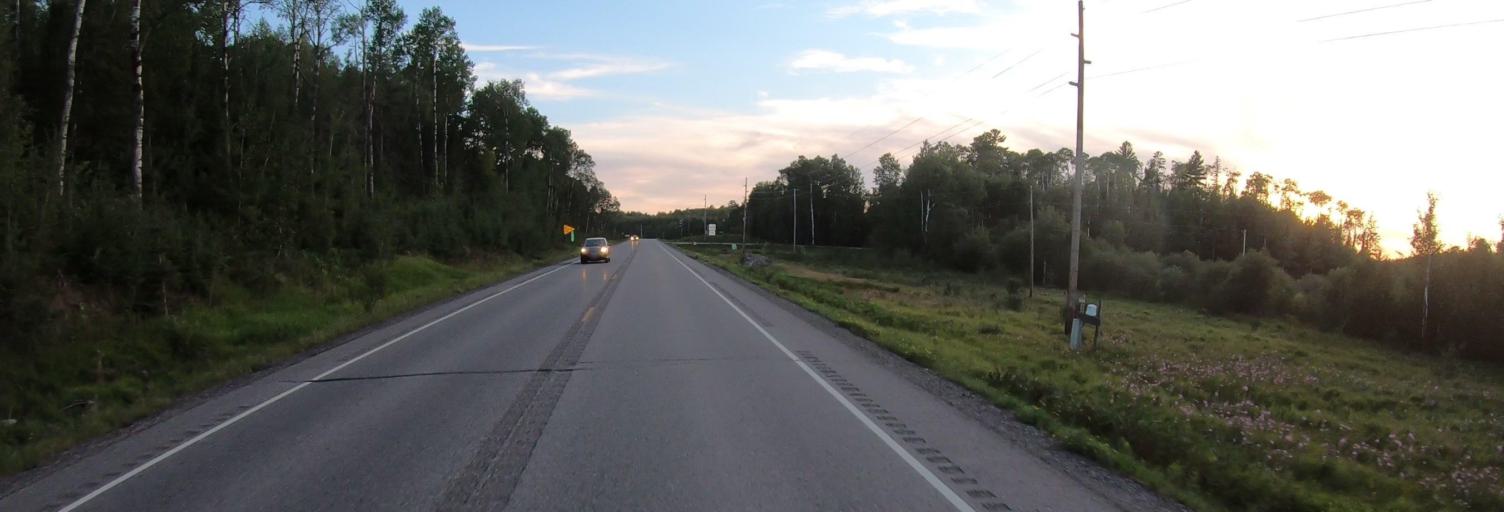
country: US
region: Minnesota
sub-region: Saint Louis County
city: Ely
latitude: 47.8820
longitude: -92.0045
